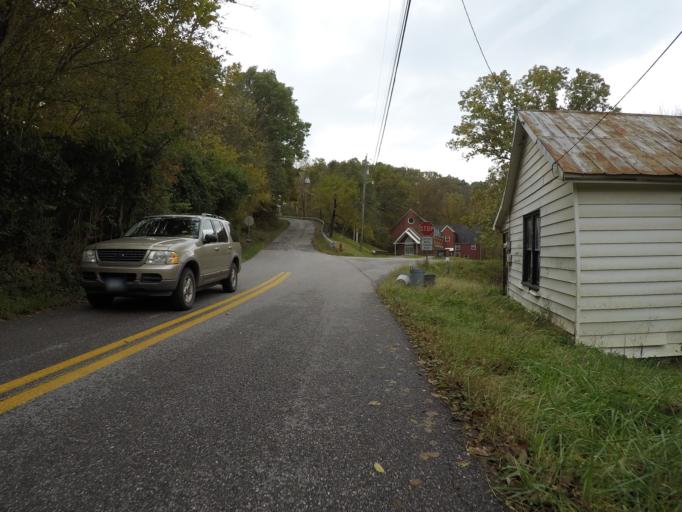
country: US
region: West Virginia
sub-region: Wayne County
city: Lavalette
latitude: 38.3655
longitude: -82.4201
